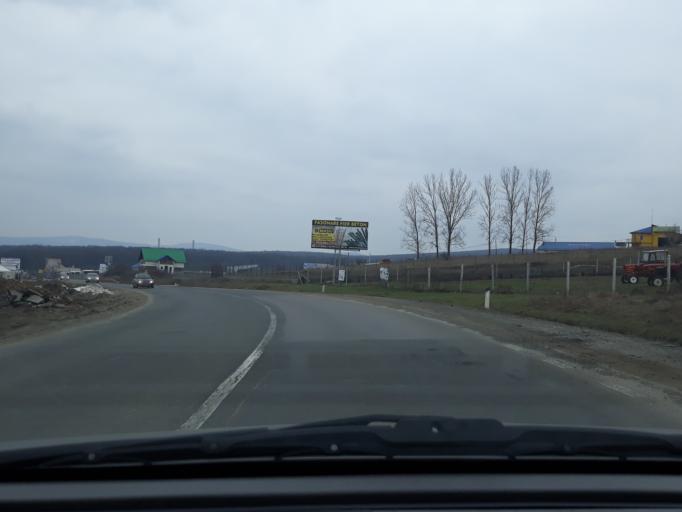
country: RO
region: Salaj
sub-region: Comuna Hereclean
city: Hereclean
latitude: 47.2302
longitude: 22.9984
